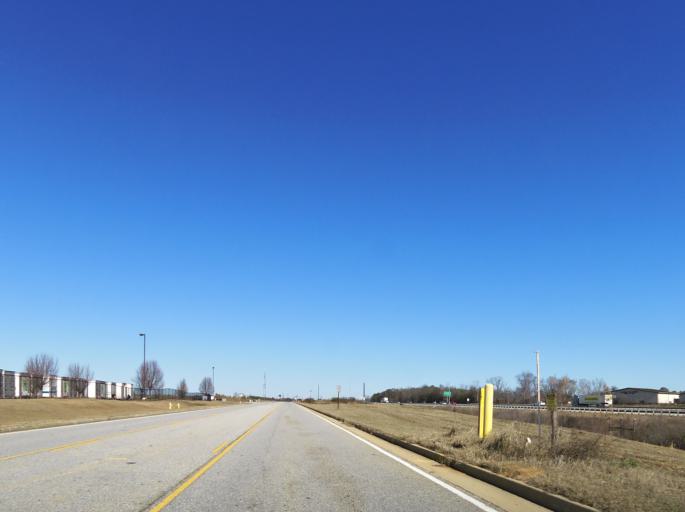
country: US
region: Georgia
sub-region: Peach County
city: Byron
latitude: 32.7297
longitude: -83.7261
